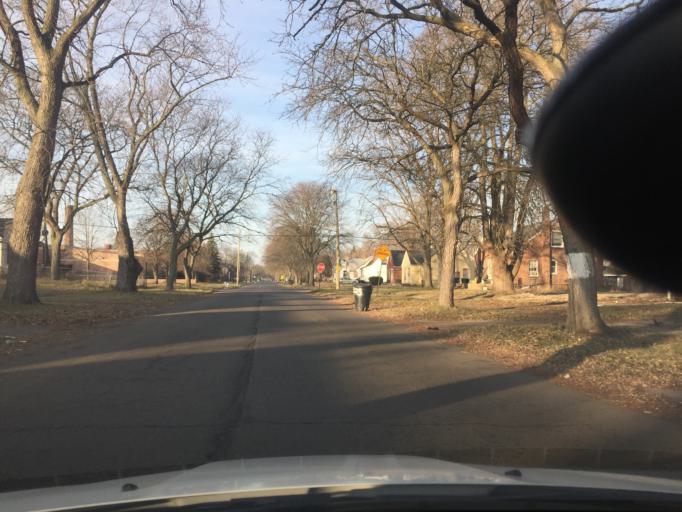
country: US
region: Michigan
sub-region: Macomb County
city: Eastpointe
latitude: 42.4428
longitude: -82.9576
